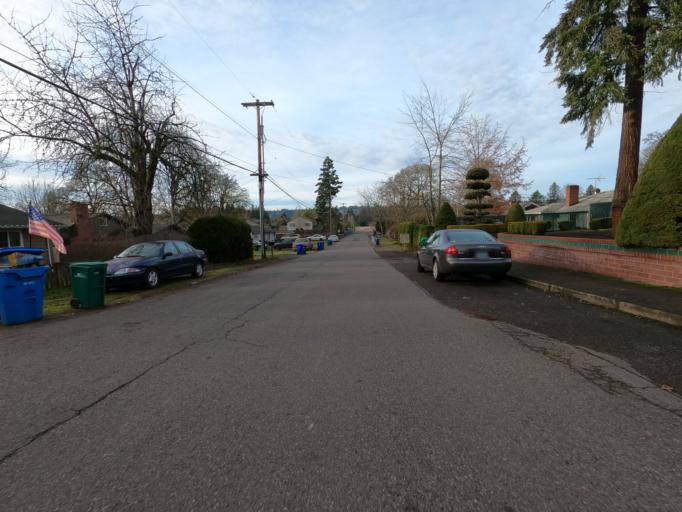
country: US
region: Oregon
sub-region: Clackamas County
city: Jennings Lodge
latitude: 45.3978
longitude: -122.6138
